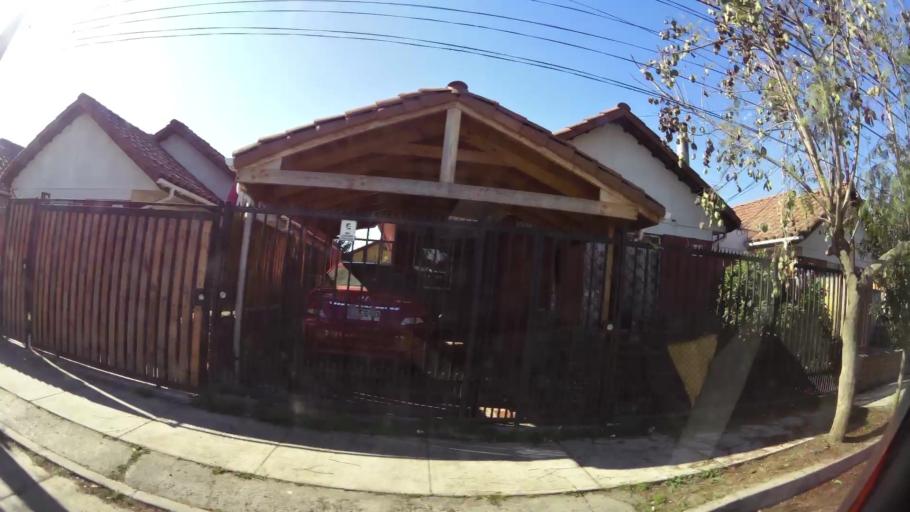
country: CL
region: Santiago Metropolitan
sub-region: Provincia de Talagante
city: Penaflor
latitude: -33.6015
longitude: -70.8736
